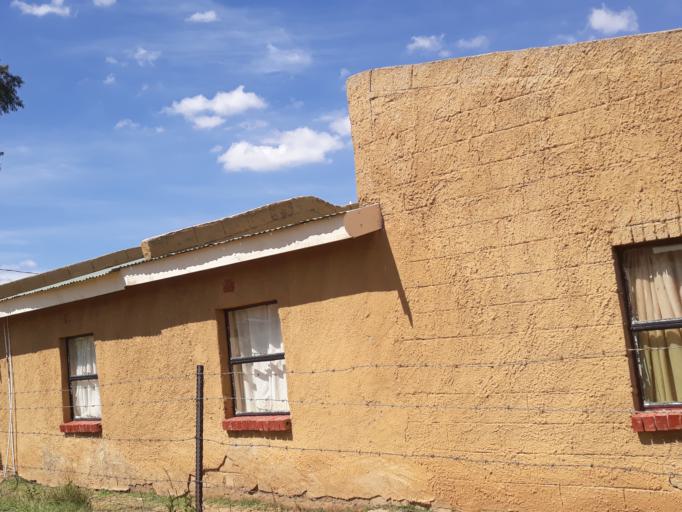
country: LS
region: Mohale's Hoek District
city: Mohale's Hoek
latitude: -30.1023
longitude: 27.4695
